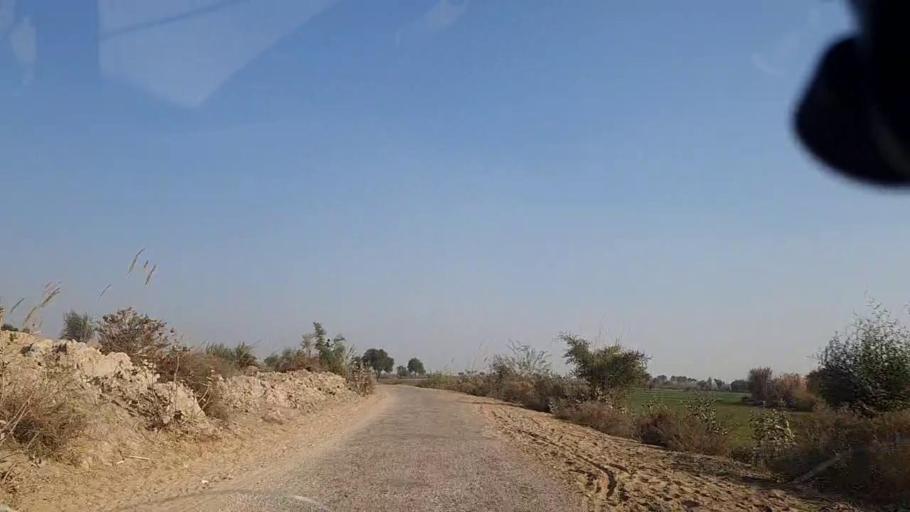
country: PK
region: Sindh
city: Khanpur
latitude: 27.6867
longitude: 69.5194
